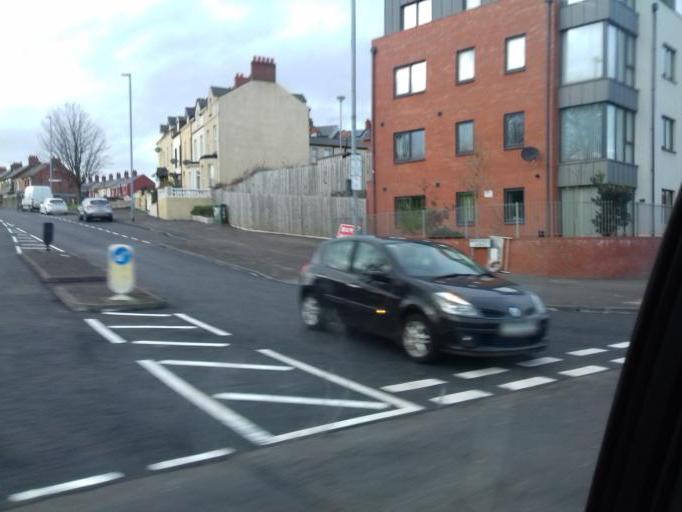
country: GB
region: Northern Ireland
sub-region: City of Belfast
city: Belfast
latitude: 54.6223
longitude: -5.9233
